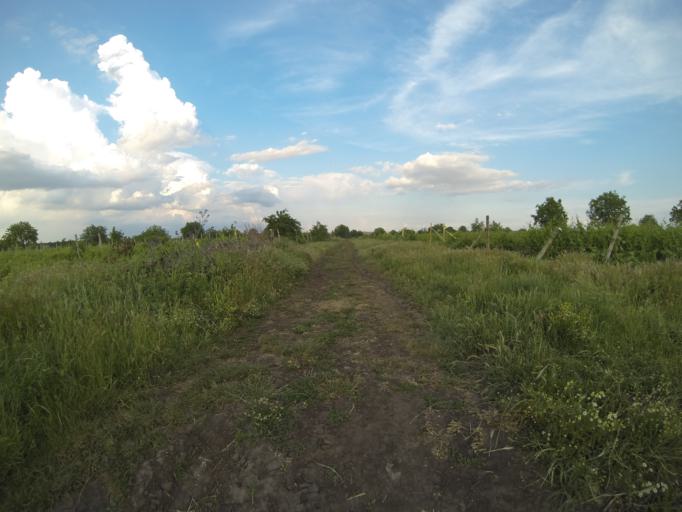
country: RO
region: Dolj
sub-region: Comuna Lipovu
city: Lipovu
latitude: 44.1141
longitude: 23.6798
